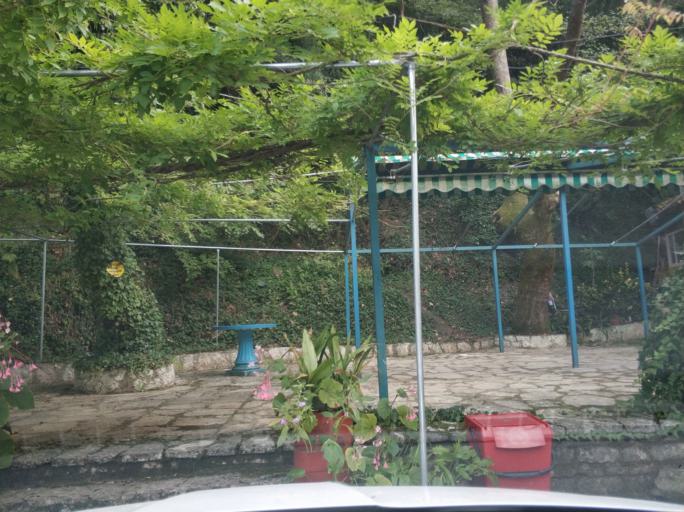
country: AL
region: Vlore
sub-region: Rrethi i Delvines
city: Mesopotam
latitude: 39.9196
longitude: 20.1705
